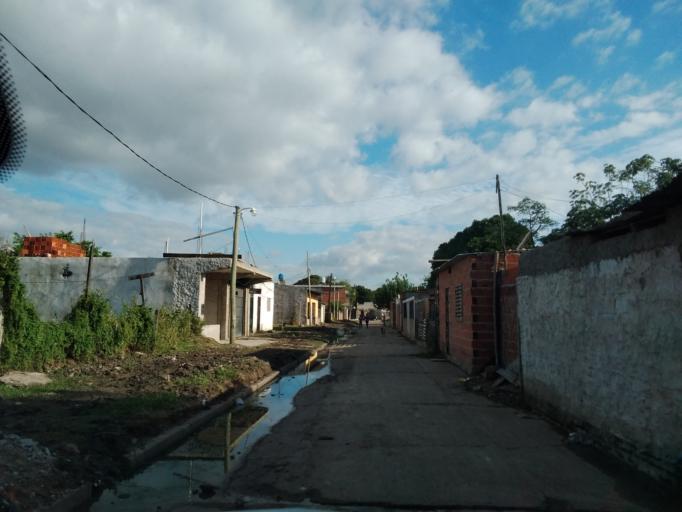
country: AR
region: Corrientes
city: Corrientes
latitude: -27.4605
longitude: -58.8173
